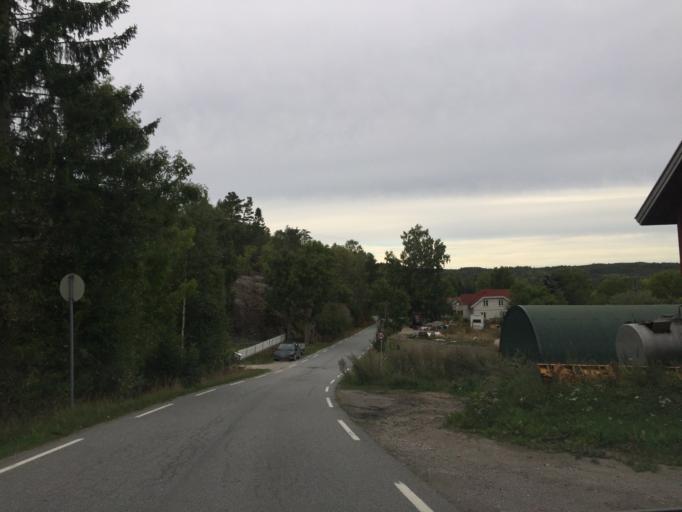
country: NO
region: Ostfold
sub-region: Hvaler
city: Skjaerhalden
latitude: 59.0585
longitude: 11.0358
